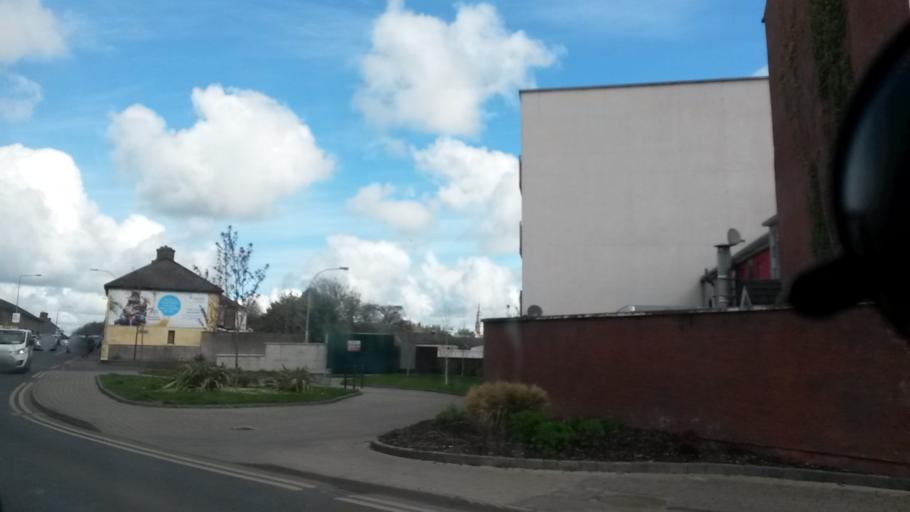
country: IE
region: Ulster
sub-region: An Cabhan
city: Cavan
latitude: 53.9874
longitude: -7.3609
